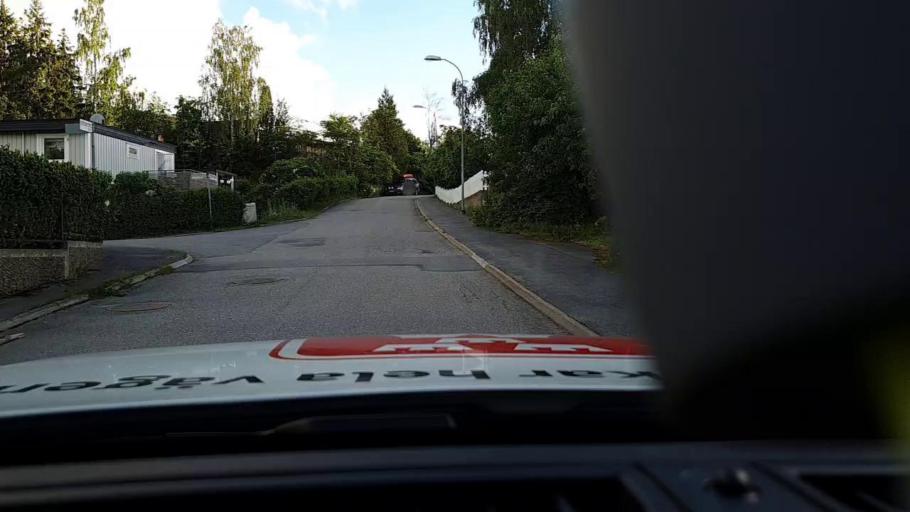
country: SE
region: Stockholm
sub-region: Huddinge Kommun
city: Huddinge
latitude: 59.2477
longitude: 17.9649
